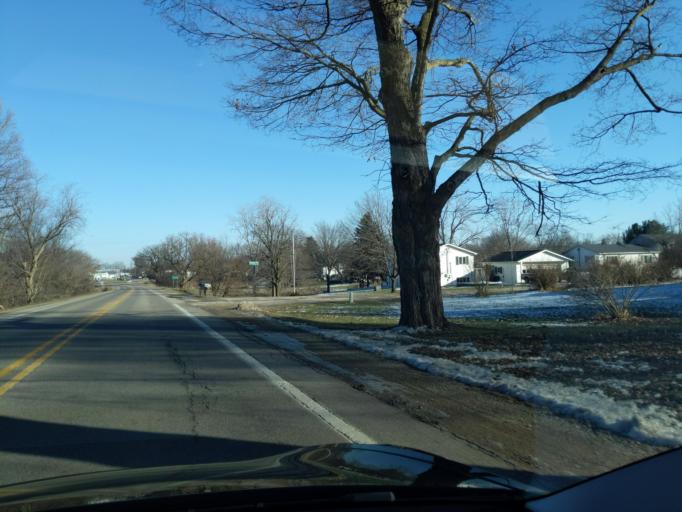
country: US
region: Michigan
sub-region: Ingham County
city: Stockbridge
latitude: 42.3937
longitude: -84.2560
